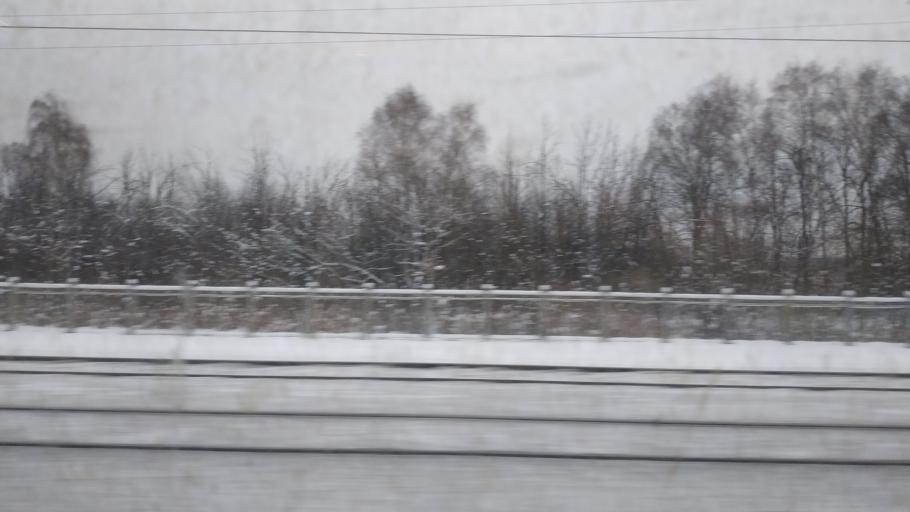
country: RU
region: Moskovskaya
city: Shcherbinka
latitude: 55.5271
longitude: 37.5671
